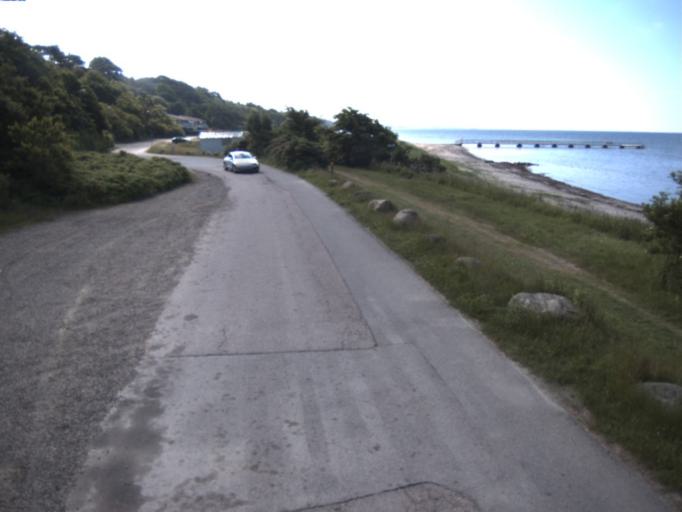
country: DK
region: Capital Region
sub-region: Helsingor Kommune
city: Helsingor
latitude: 56.0908
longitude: 12.6457
